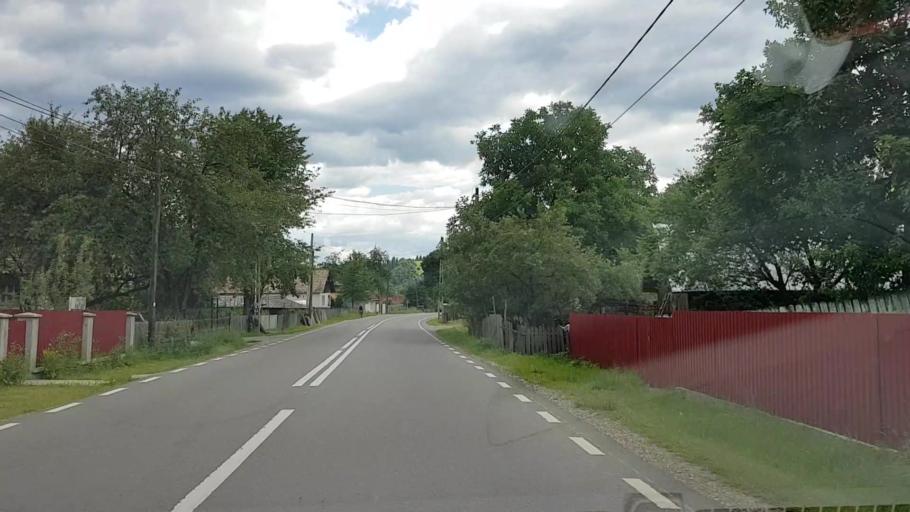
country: RO
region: Neamt
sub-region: Comuna Farcasa
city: Farcasa
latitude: 47.1630
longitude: 25.8131
